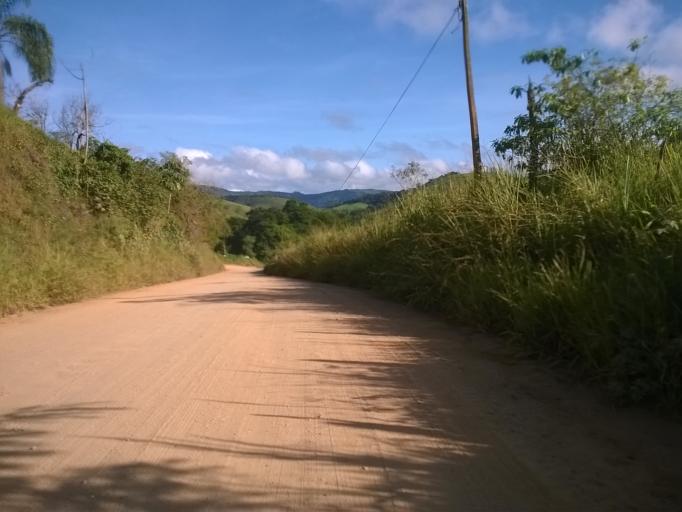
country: BR
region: Minas Gerais
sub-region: Uba
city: Uba
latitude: -21.0810
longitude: -42.9818
